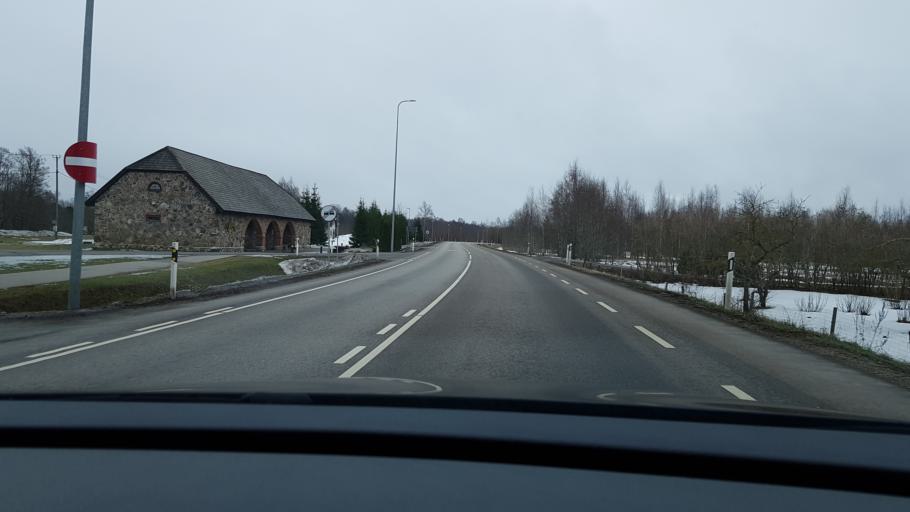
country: EE
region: Paernumaa
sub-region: Sauga vald
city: Sauga
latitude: 58.4296
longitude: 24.4385
